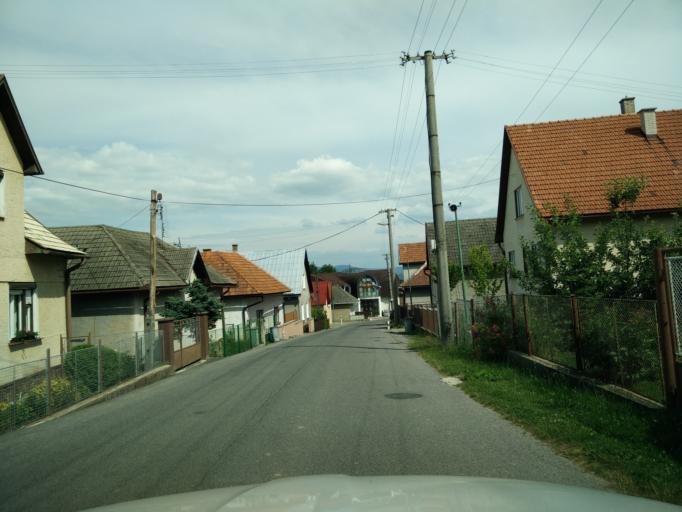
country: SK
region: Nitriansky
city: Bojnice
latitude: 48.8324
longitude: 18.5912
